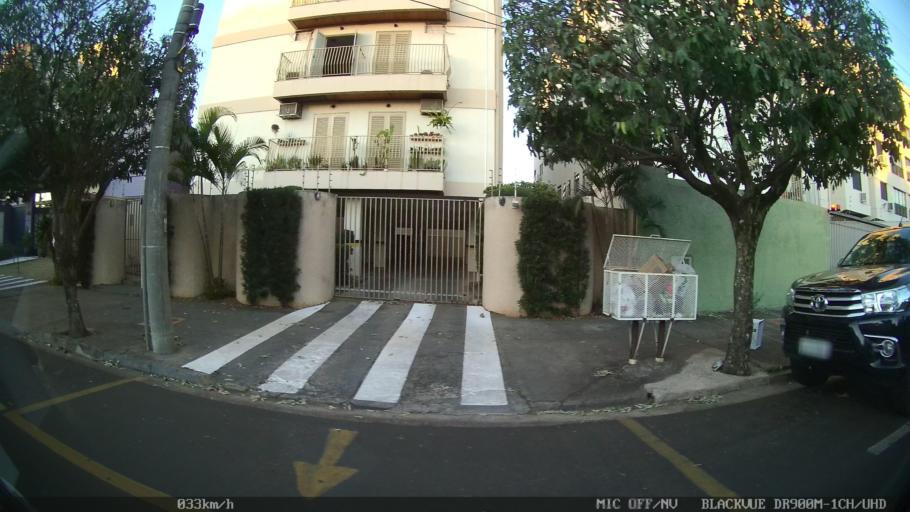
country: BR
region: Sao Paulo
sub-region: Sao Jose Do Rio Preto
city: Sao Jose do Rio Preto
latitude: -20.8459
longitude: -49.3934
